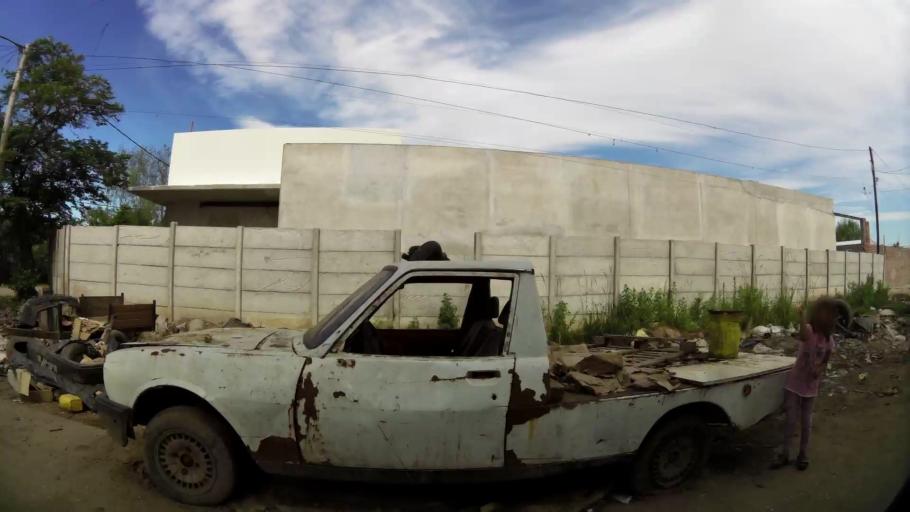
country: AR
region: Santa Fe
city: Granadero Baigorria
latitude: -32.9111
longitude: -60.7048
